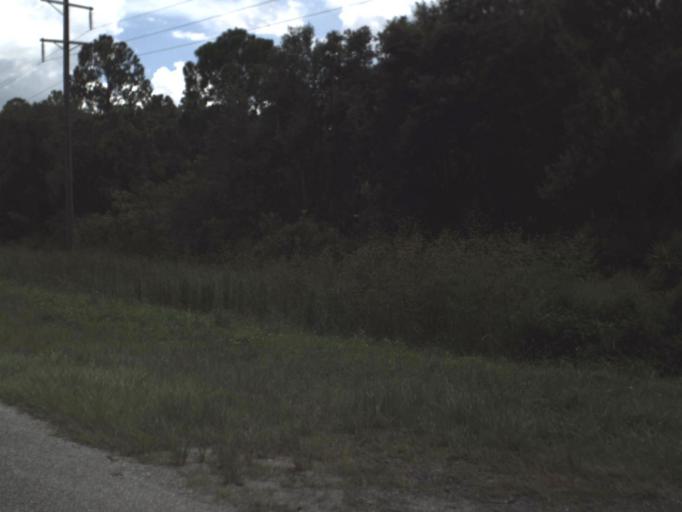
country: US
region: Florida
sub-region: Polk County
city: Babson Park
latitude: 27.8744
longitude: -81.4004
